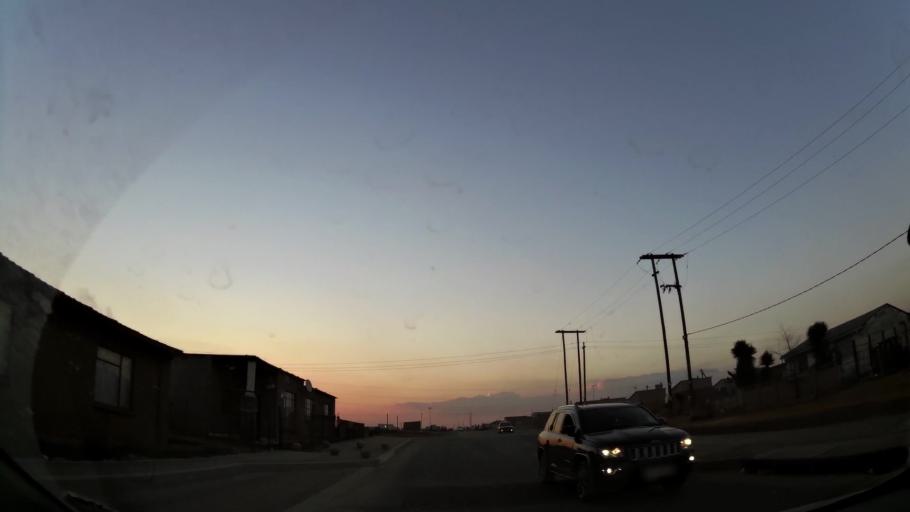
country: ZA
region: Gauteng
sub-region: Ekurhuleni Metropolitan Municipality
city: Nigel
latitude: -26.3713
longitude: 28.3996
